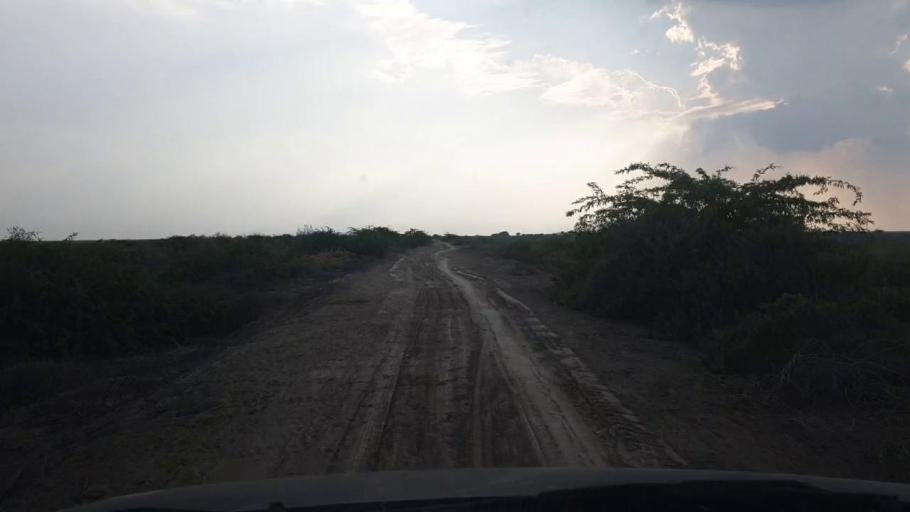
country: PK
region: Sindh
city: Badin
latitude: 24.4710
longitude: 68.6969
